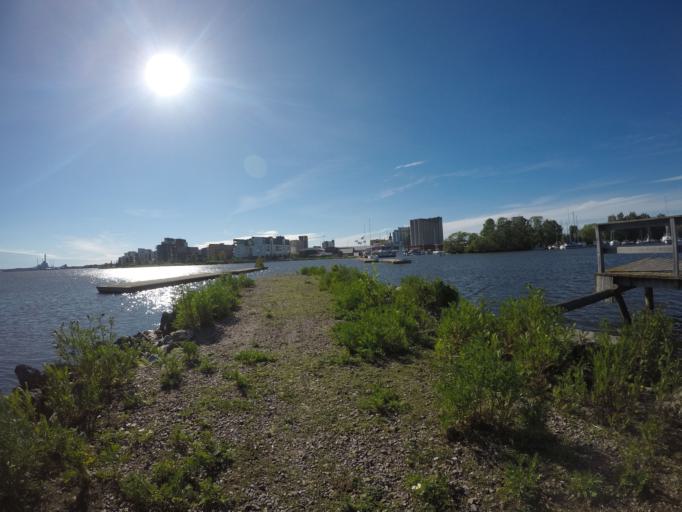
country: SE
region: Vaestmanland
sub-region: Vasteras
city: Vasteras
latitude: 59.6039
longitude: 16.5668
